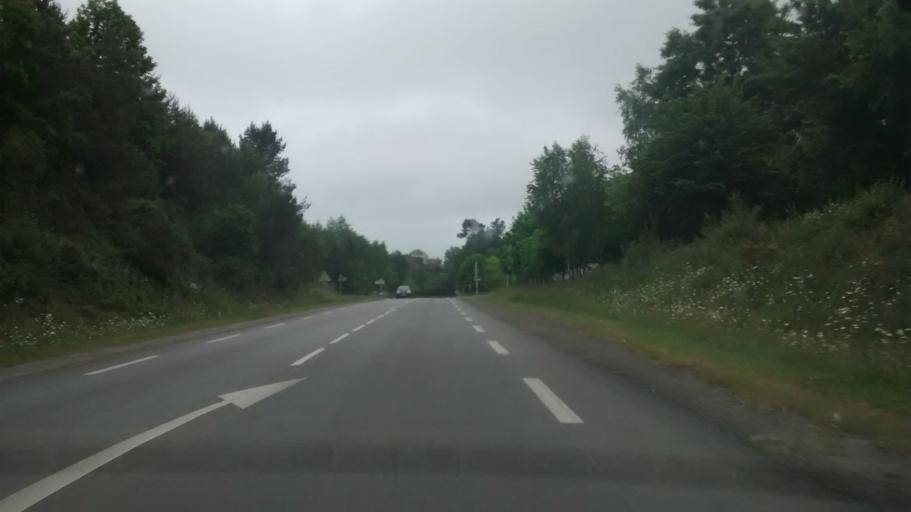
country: FR
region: Brittany
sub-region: Departement du Morbihan
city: Molac
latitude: 47.7766
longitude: -2.4413
